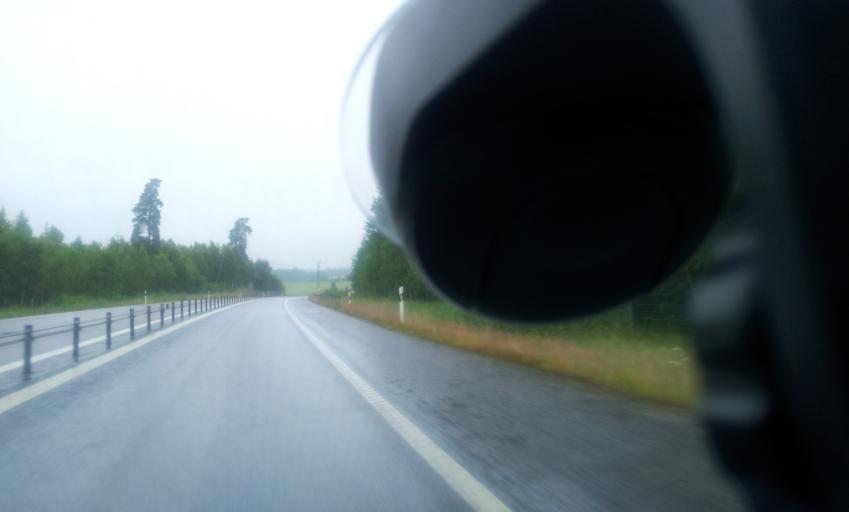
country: SE
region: OEstergoetland
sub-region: Soderkopings Kommun
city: Soederkoeping
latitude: 58.4440
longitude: 16.3681
